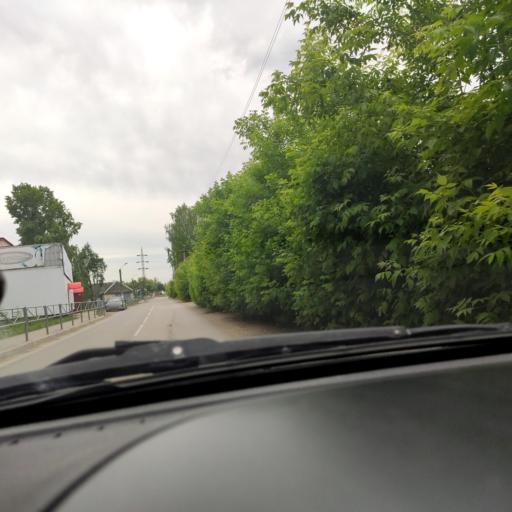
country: RU
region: Perm
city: Overyata
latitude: 58.0635
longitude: 55.8214
